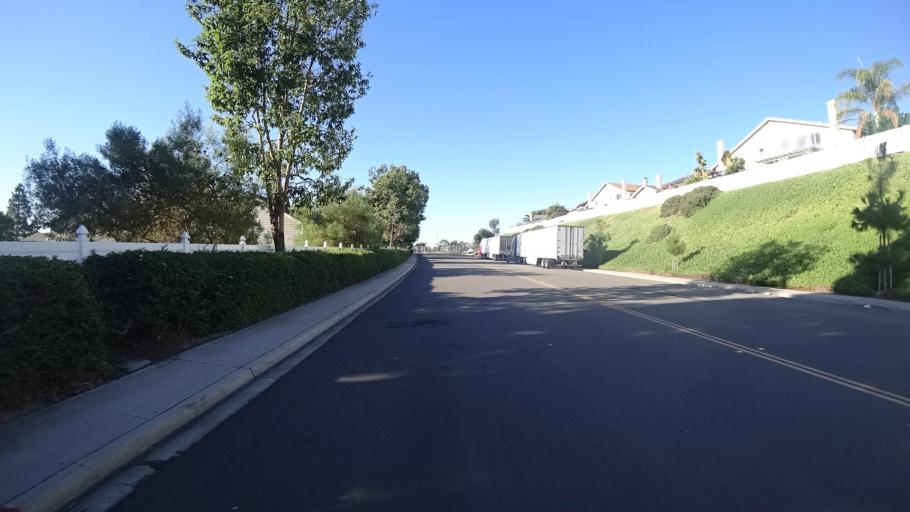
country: US
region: California
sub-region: San Diego County
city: Bonita
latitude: 32.6838
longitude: -117.0338
